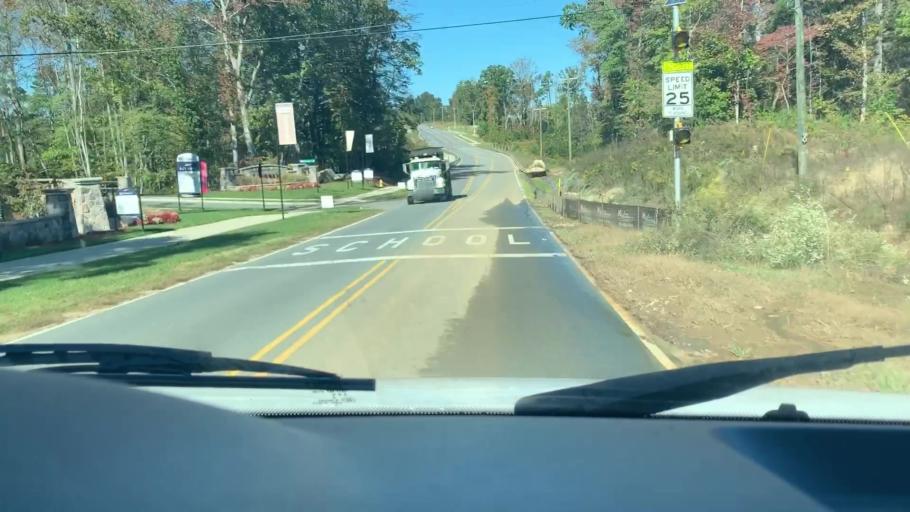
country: US
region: North Carolina
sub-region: Gaston County
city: Davidson
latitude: 35.4663
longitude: -80.8228
